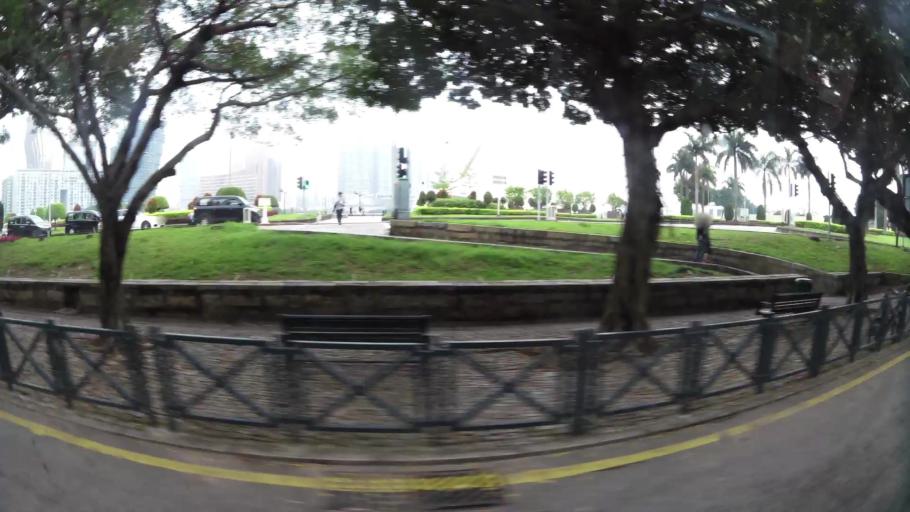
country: MO
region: Macau
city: Macau
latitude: 22.1866
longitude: 113.5374
